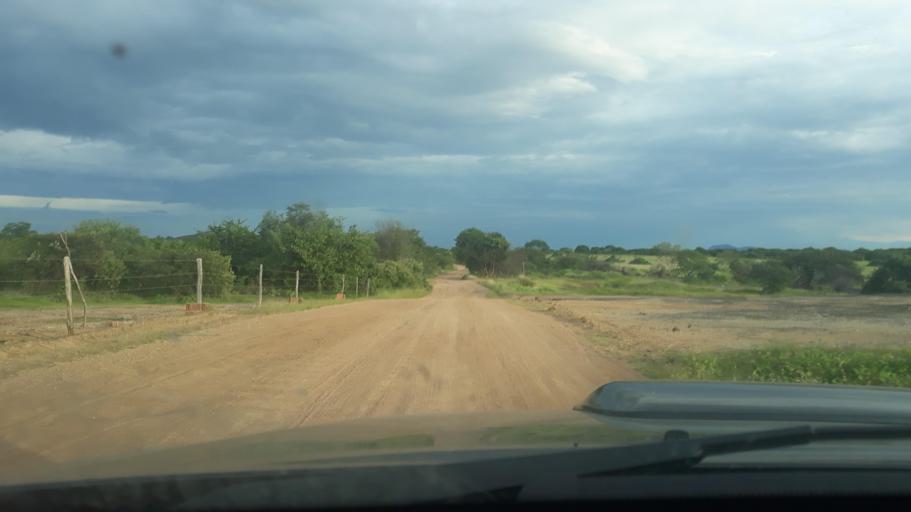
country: BR
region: Bahia
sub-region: Riacho De Santana
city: Riacho de Santana
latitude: -13.9071
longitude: -42.9678
